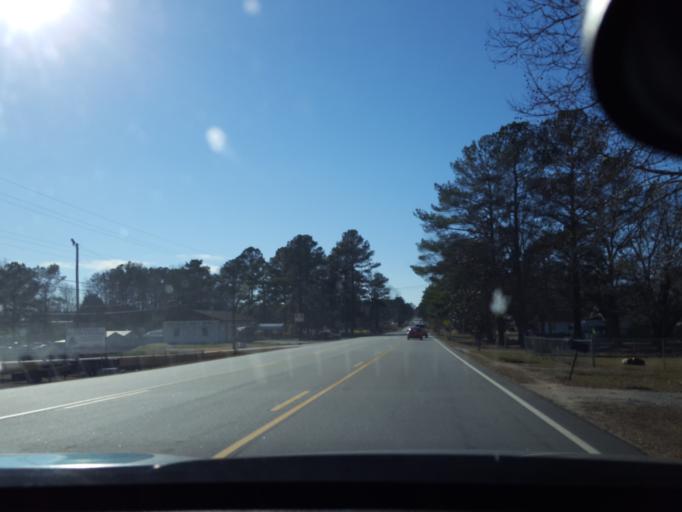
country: US
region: North Carolina
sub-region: Halifax County
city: South Rosemary
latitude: 36.4468
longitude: -77.7383
